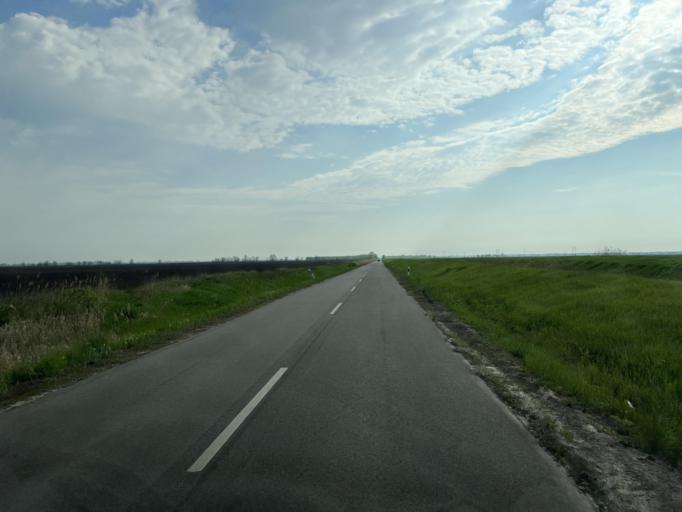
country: HU
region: Pest
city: Jaszkarajeno
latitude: 47.1083
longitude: 20.0465
